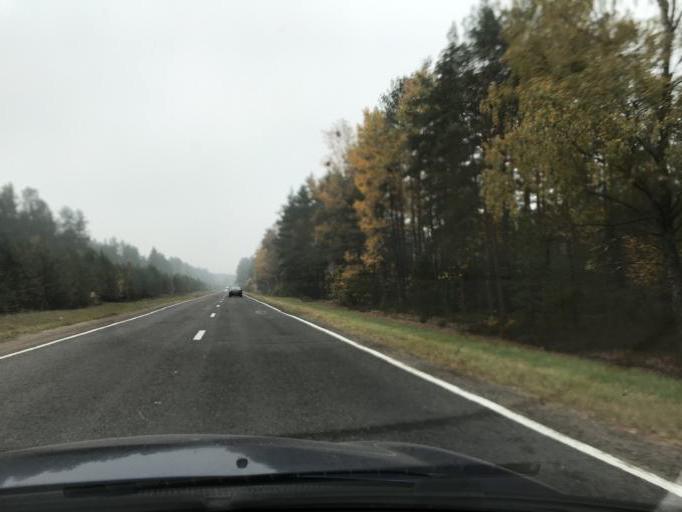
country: LT
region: Alytaus apskritis
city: Druskininkai
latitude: 53.8939
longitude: 23.9125
